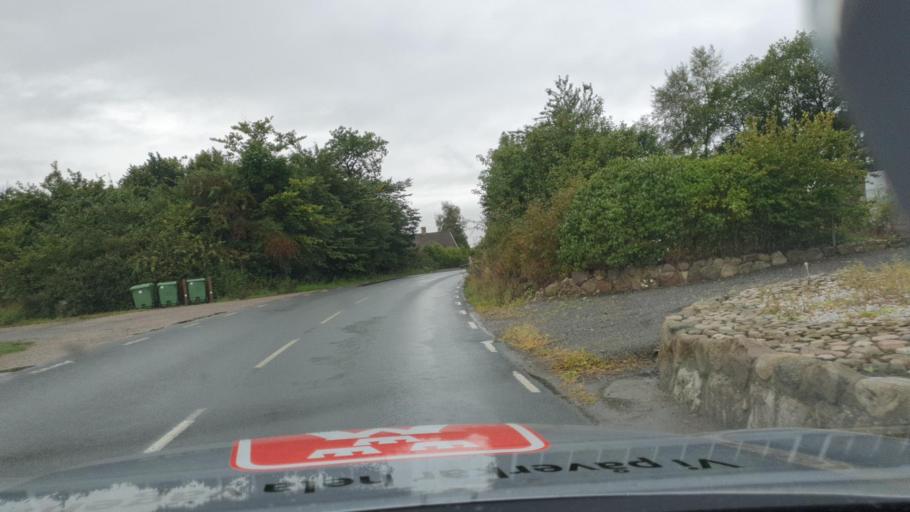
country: SE
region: Skane
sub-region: Simrishamns Kommun
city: Kivik
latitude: 55.5794
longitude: 14.1378
